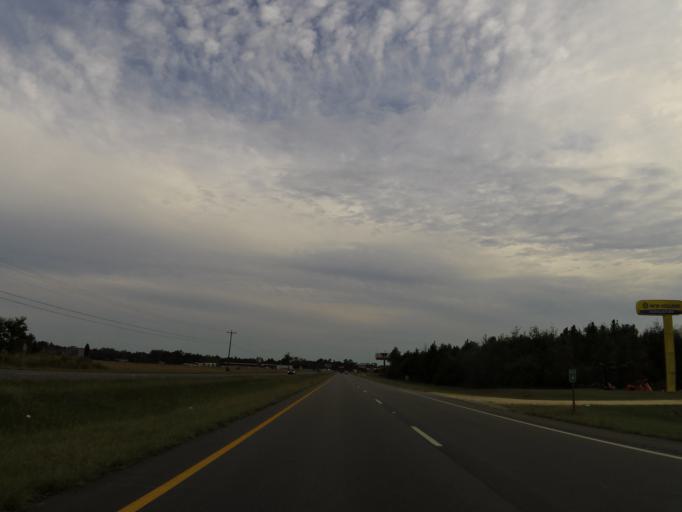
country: US
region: Alabama
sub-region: Escambia County
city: Atmore
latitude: 31.0548
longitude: -87.4930
